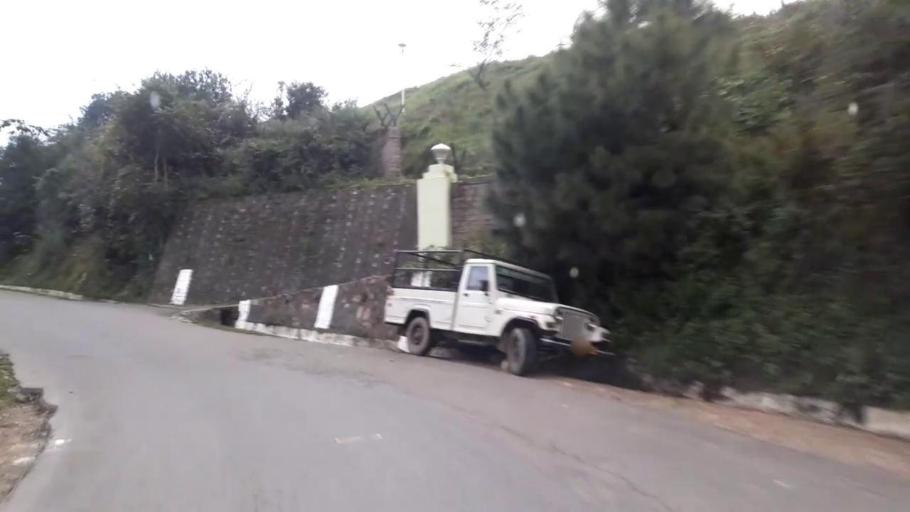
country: IN
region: Himachal Pradesh
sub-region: Shimla
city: Jutogh
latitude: 31.0474
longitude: 77.1349
